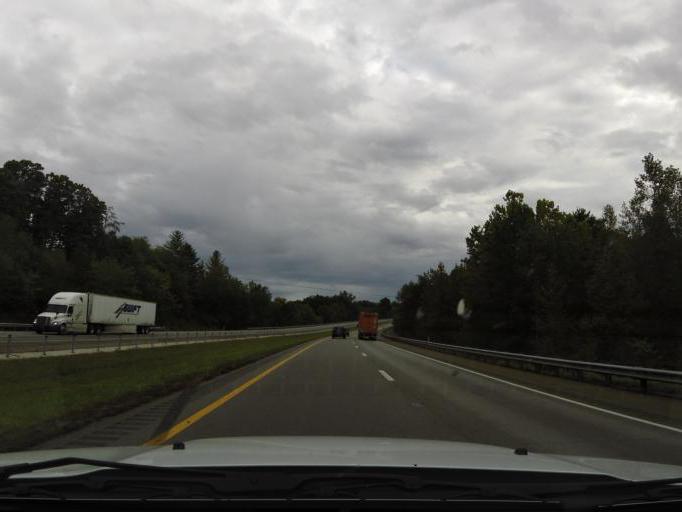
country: US
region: Kentucky
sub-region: Whitley County
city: Corbin
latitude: 36.8828
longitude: -84.1507
